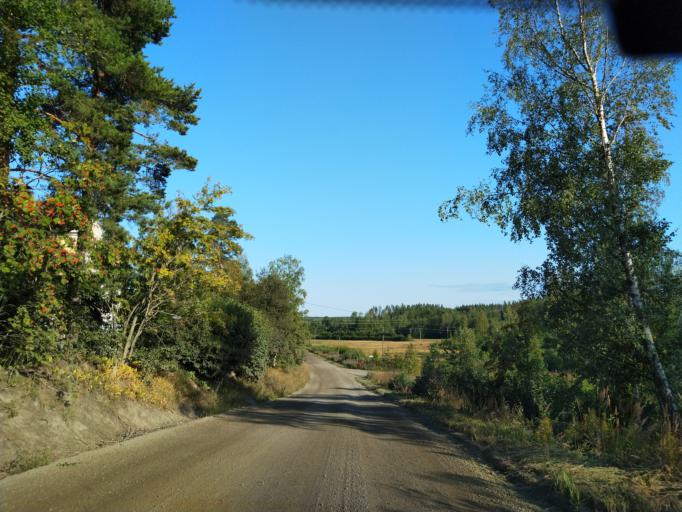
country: FI
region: Central Finland
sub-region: Jaemsae
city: Kuhmoinen
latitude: 61.6020
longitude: 25.1510
